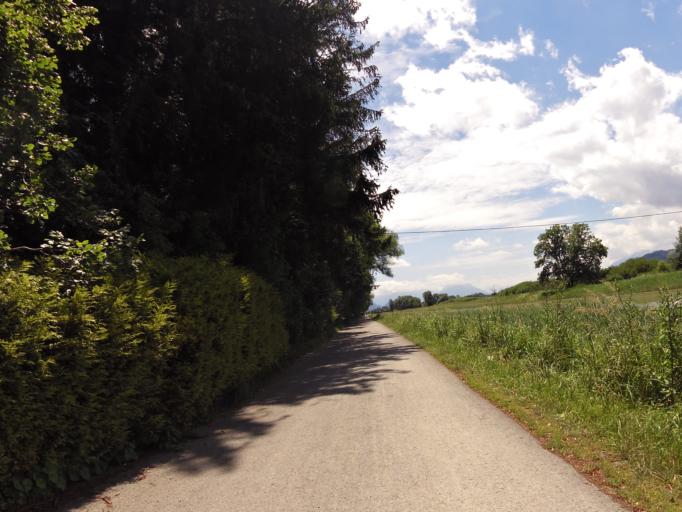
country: AT
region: Vorarlberg
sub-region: Politischer Bezirk Bregenz
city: Hard
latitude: 47.4875
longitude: 9.6754
